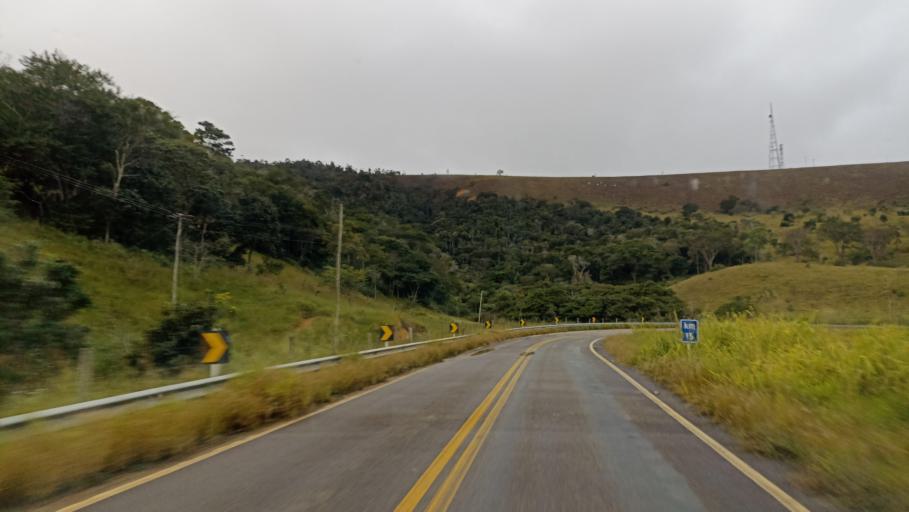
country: BR
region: Minas Gerais
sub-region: Joaima
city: Joaima
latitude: -16.6804
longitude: -40.5220
